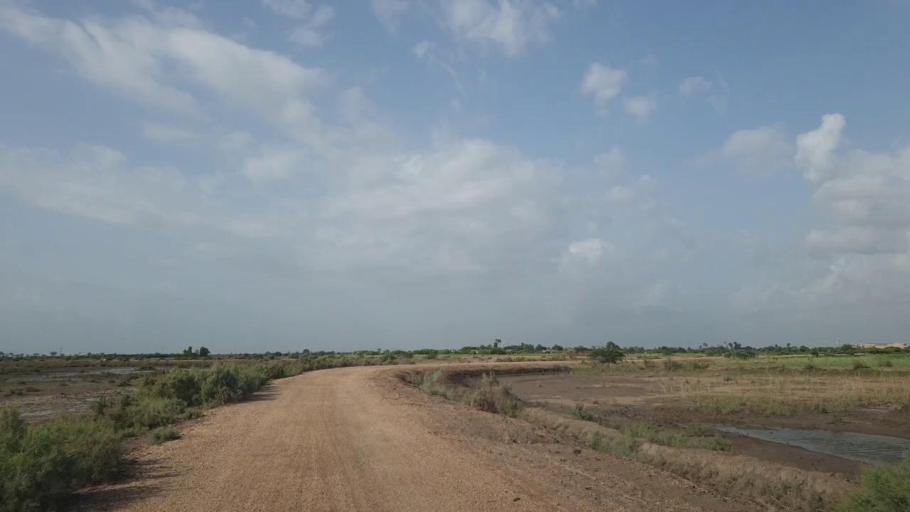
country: PK
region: Sindh
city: Kadhan
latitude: 24.6327
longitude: 69.0880
